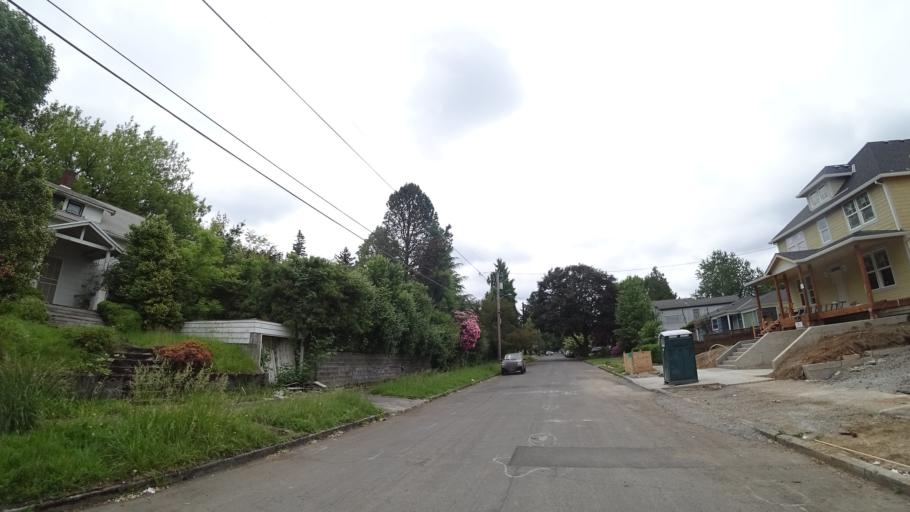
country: US
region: Oregon
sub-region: Clackamas County
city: Milwaukie
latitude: 45.4866
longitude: -122.6237
